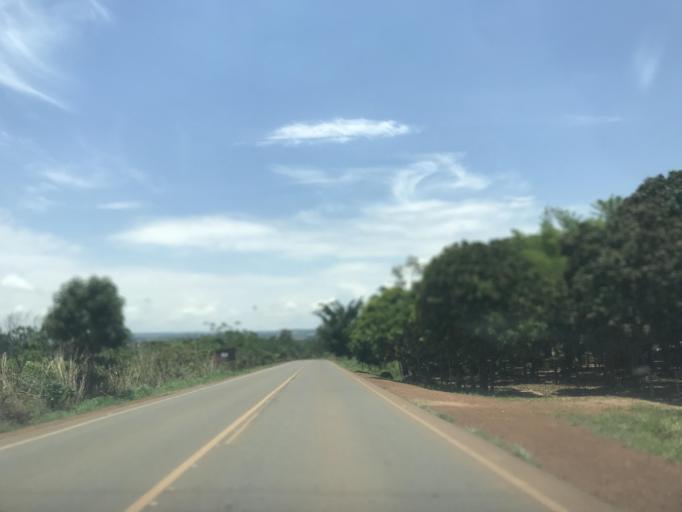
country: BR
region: Goias
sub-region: Vianopolis
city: Vianopolis
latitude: -16.5967
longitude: -48.3477
